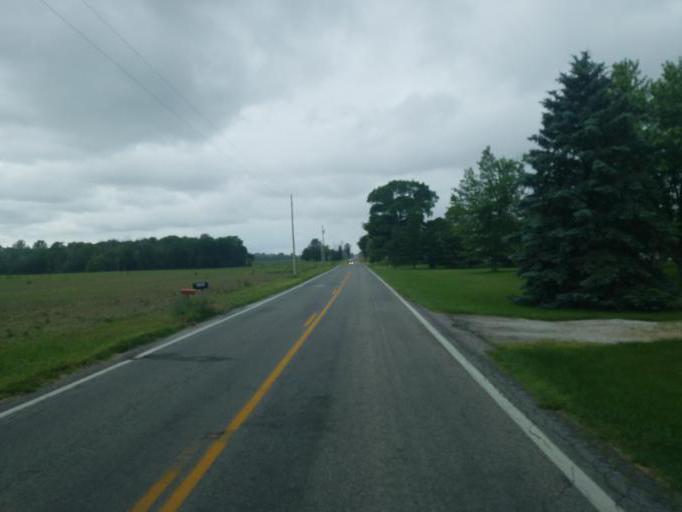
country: US
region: Ohio
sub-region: Morrow County
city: Cardington
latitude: 40.5347
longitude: -82.9910
